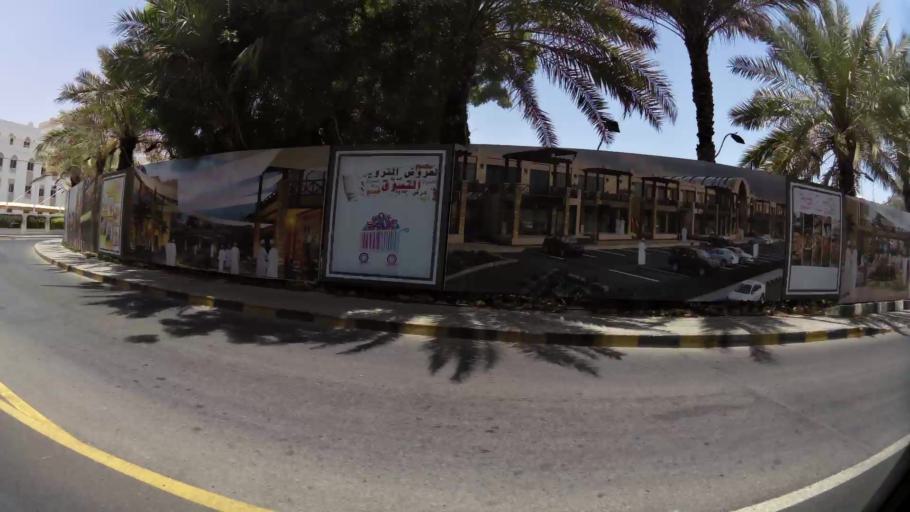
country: OM
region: Muhafazat Masqat
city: Bawshar
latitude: 23.5994
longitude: 58.4557
